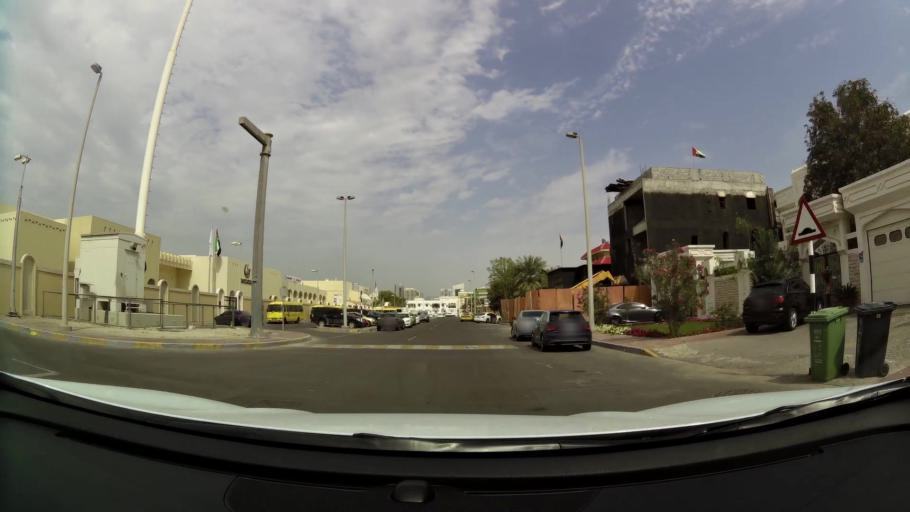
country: AE
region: Abu Dhabi
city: Abu Dhabi
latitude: 24.4581
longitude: 54.3678
